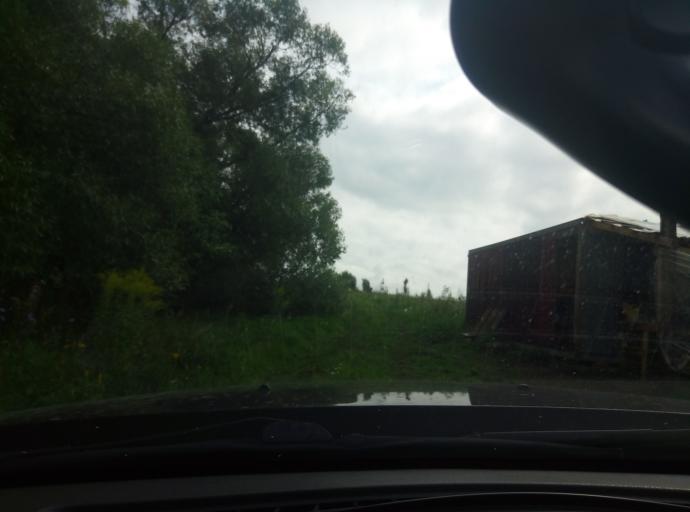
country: RU
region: Tula
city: Shvartsevskiy
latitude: 54.0840
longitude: 38.0207
